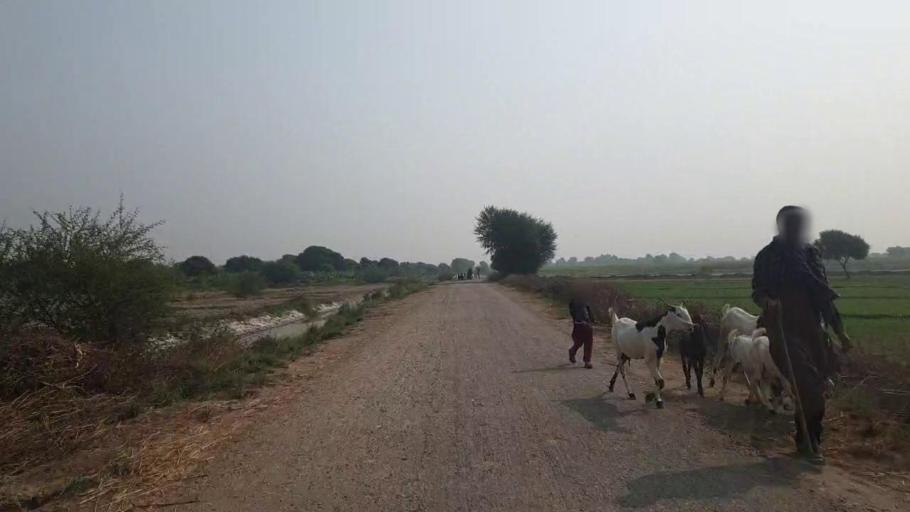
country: PK
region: Sindh
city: Tando Muhammad Khan
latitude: 25.2468
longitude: 68.5600
